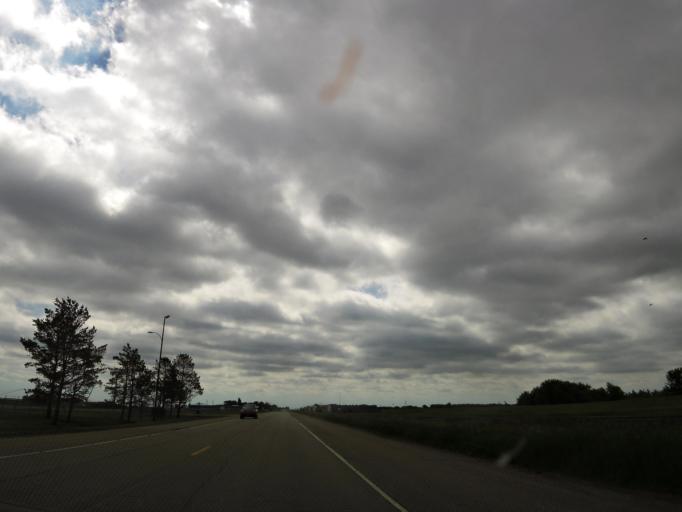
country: US
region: Minnesota
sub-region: Polk County
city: East Grand Forks
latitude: 47.9219
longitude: -97.0002
